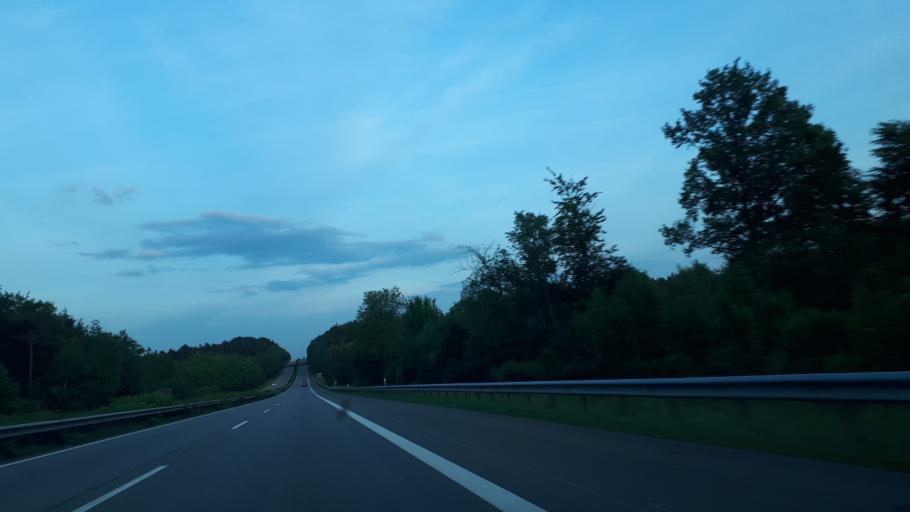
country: DE
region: Rheinland-Pfalz
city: Laubach
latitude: 50.2317
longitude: 7.0918
